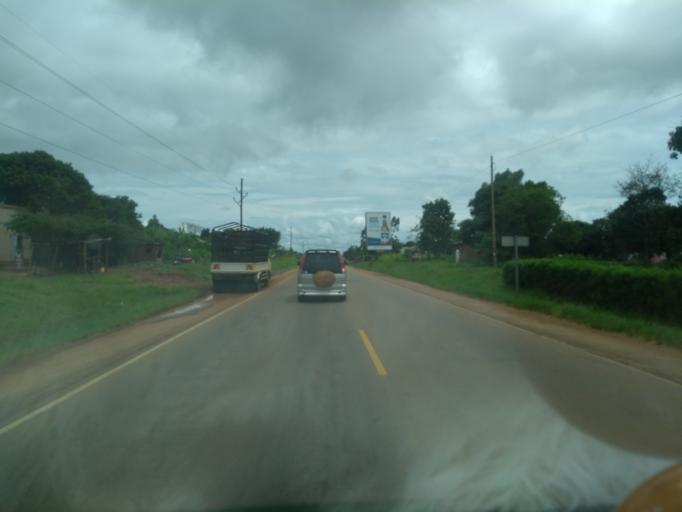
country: UG
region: Central Region
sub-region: Butambala District
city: Gombe
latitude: -0.0027
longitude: 32.0381
